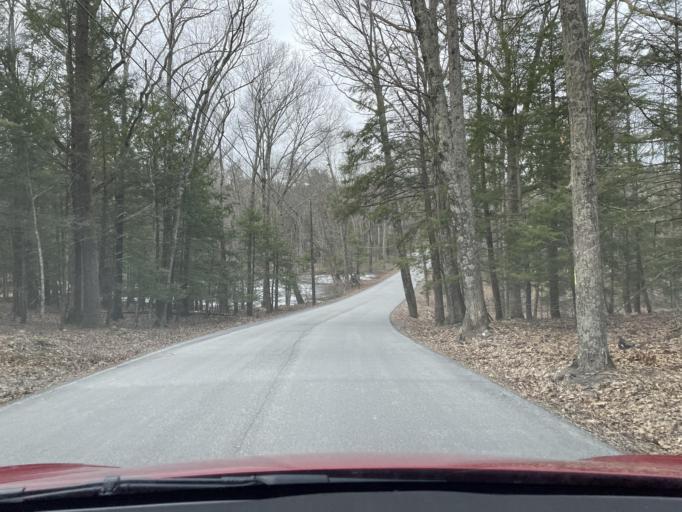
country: US
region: New York
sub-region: Ulster County
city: Saugerties
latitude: 42.1080
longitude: -73.9925
